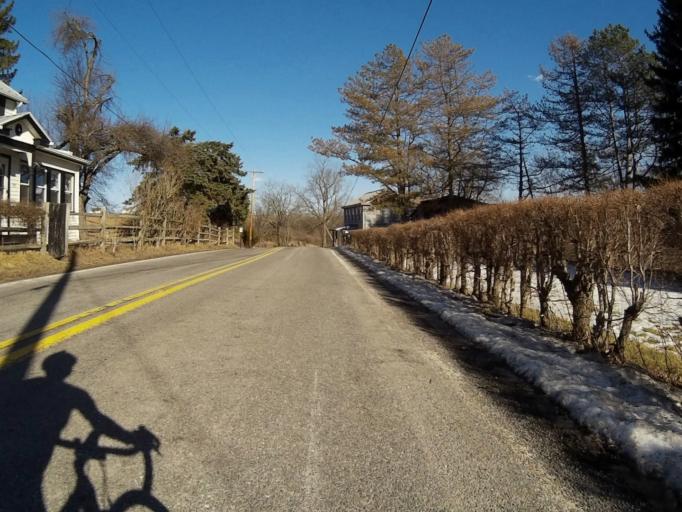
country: US
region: Pennsylvania
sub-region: Centre County
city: Park Forest Village
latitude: 40.8346
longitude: -77.9429
